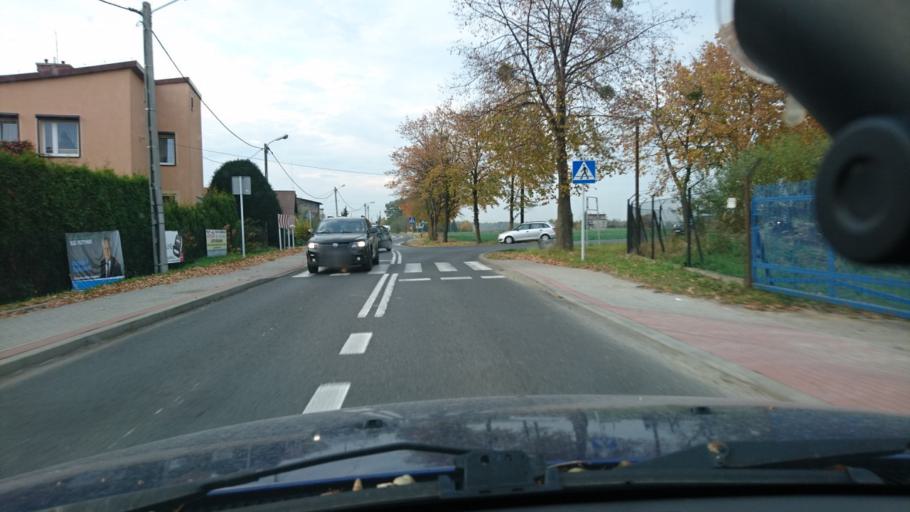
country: PL
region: Silesian Voivodeship
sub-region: Powiat bielski
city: Kozy
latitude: 49.8455
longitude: 19.1173
